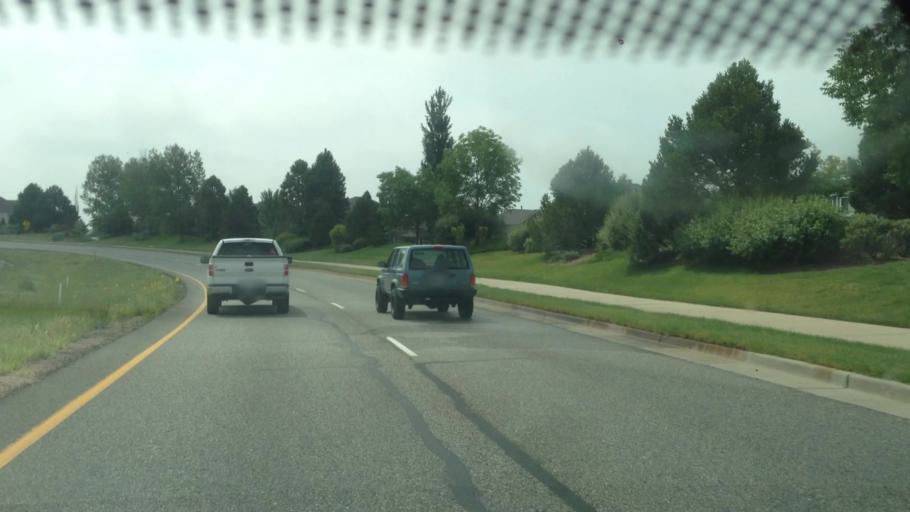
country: US
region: Colorado
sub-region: Douglas County
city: Parker
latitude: 39.6023
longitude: -104.7260
